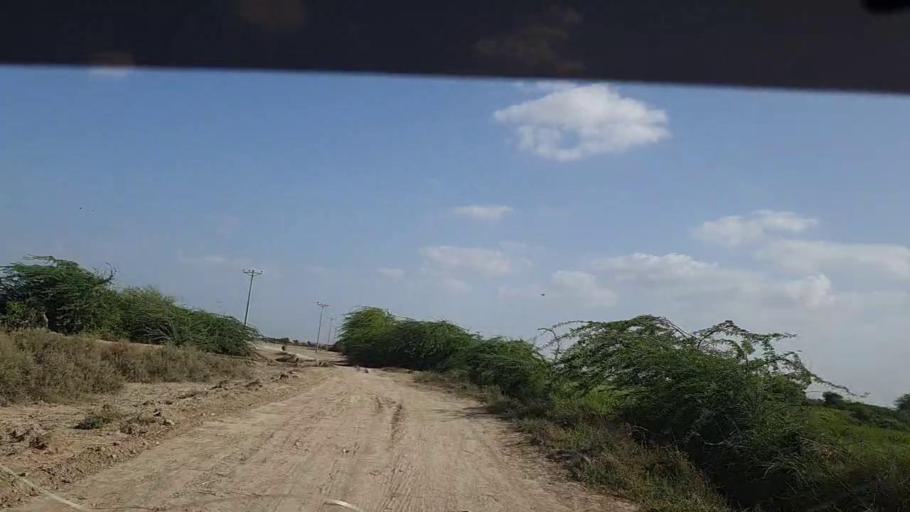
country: PK
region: Sindh
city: Kadhan
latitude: 24.4612
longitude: 68.8536
